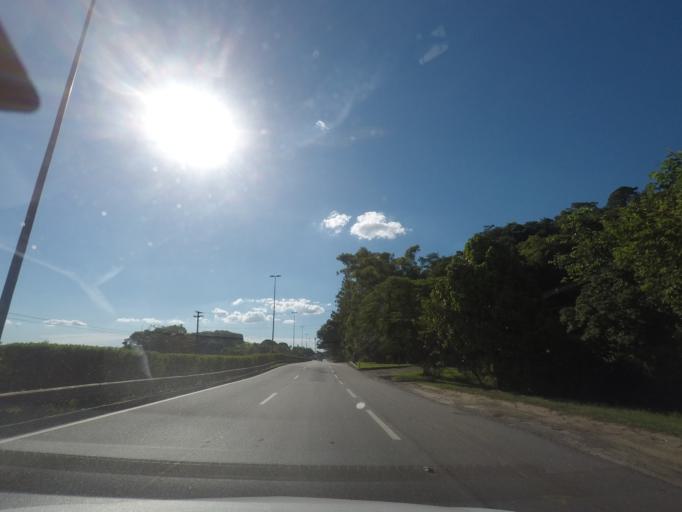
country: BR
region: Rio de Janeiro
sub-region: Sao Goncalo
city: Sao Goncalo
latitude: -22.6647
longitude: -43.1102
